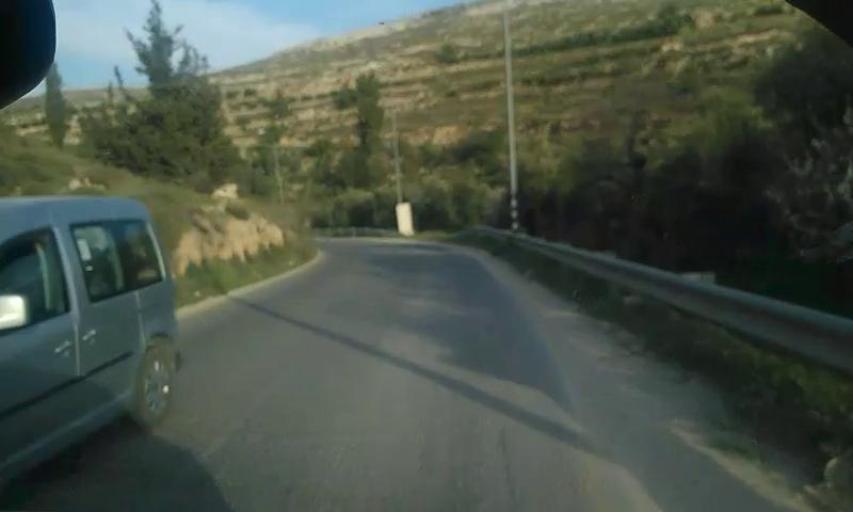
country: PS
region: West Bank
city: Marah Rabbah
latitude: 31.6013
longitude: 35.1828
